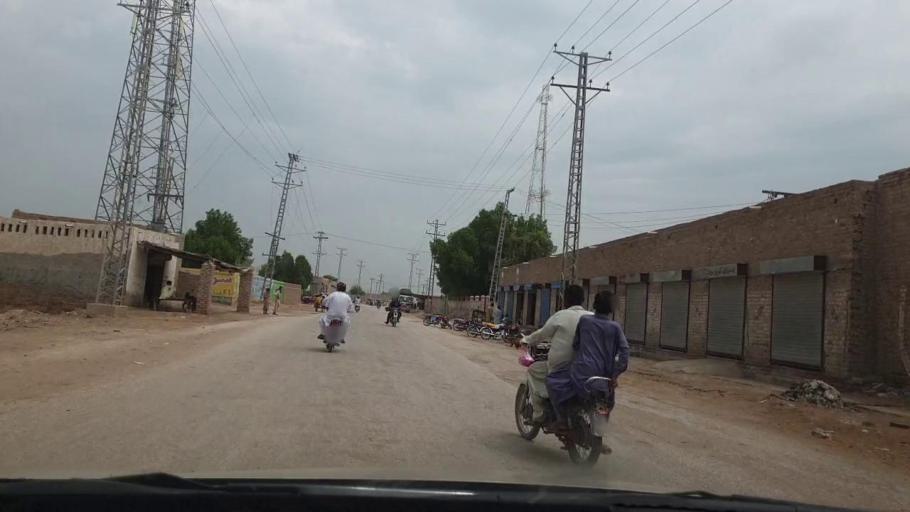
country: PK
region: Sindh
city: Ratodero
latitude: 27.8041
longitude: 68.2996
